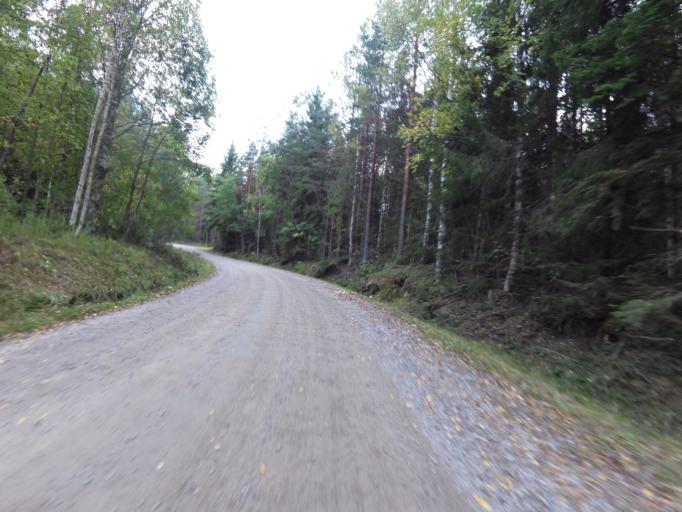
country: SE
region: Gaevleborg
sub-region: Sandvikens Kommun
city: Sandviken
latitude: 60.7559
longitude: 16.8426
